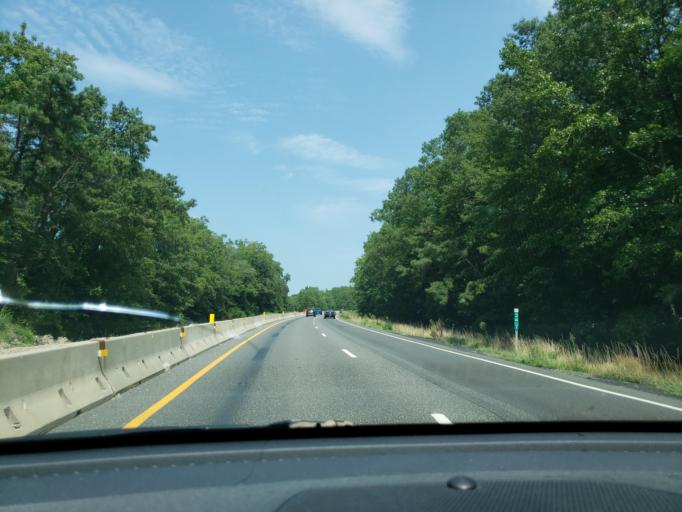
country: US
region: New Jersey
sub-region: Atlantic County
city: Northfield
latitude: 39.3827
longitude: -74.5763
